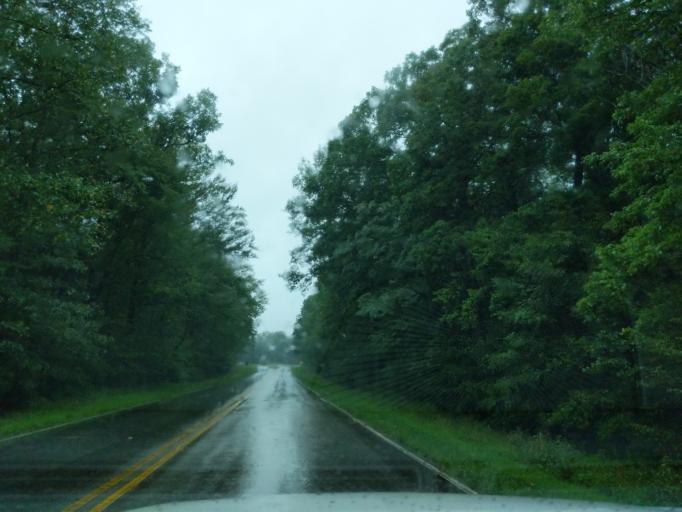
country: US
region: Kentucky
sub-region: Barren County
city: Cave City
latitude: 37.1831
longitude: -86.0942
